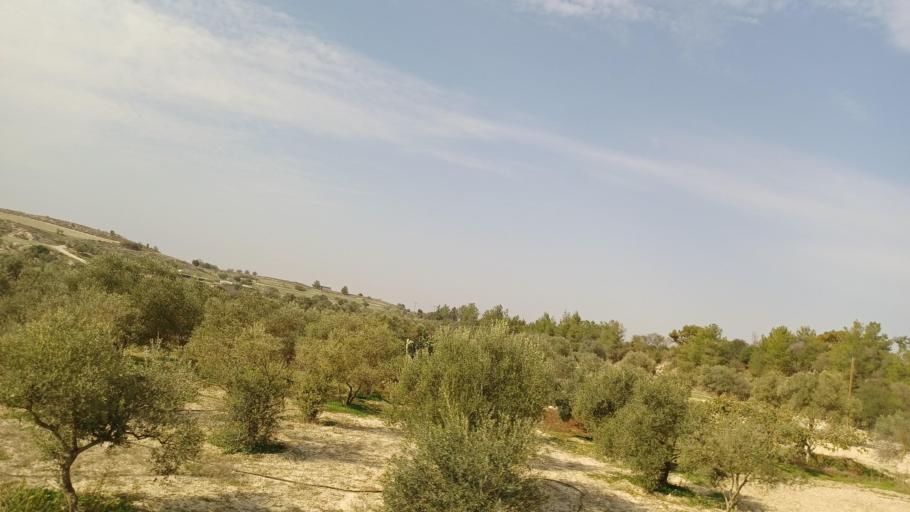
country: CY
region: Lefkosia
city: Lympia
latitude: 34.9906
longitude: 33.4564
